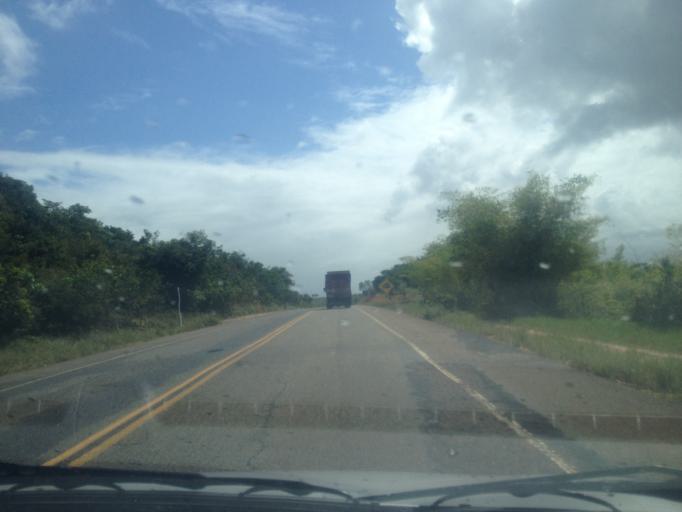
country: BR
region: Sergipe
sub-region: Indiaroba
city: Indiaroba
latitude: -11.5734
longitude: -37.5483
